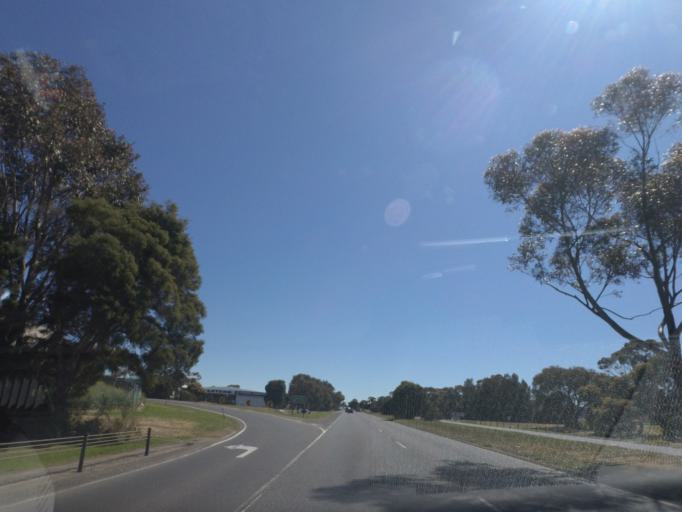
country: AU
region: Victoria
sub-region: Hume
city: Craigieburn
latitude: -37.6053
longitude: 144.9454
